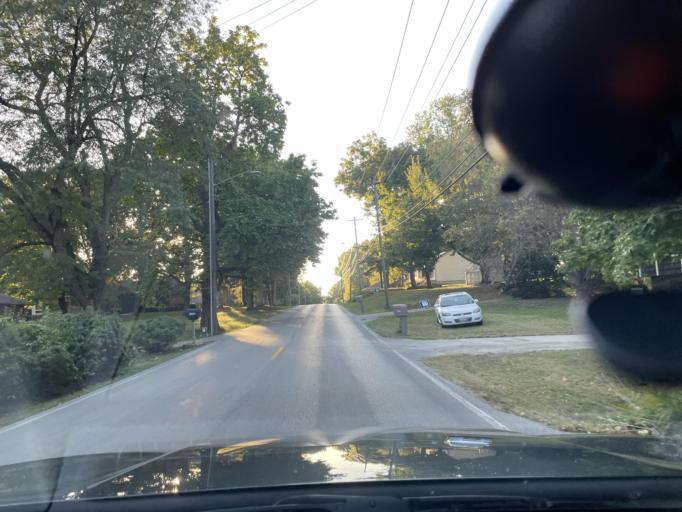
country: US
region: Missouri
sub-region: Andrew County
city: Country Club Village
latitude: 39.7994
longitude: -94.8220
